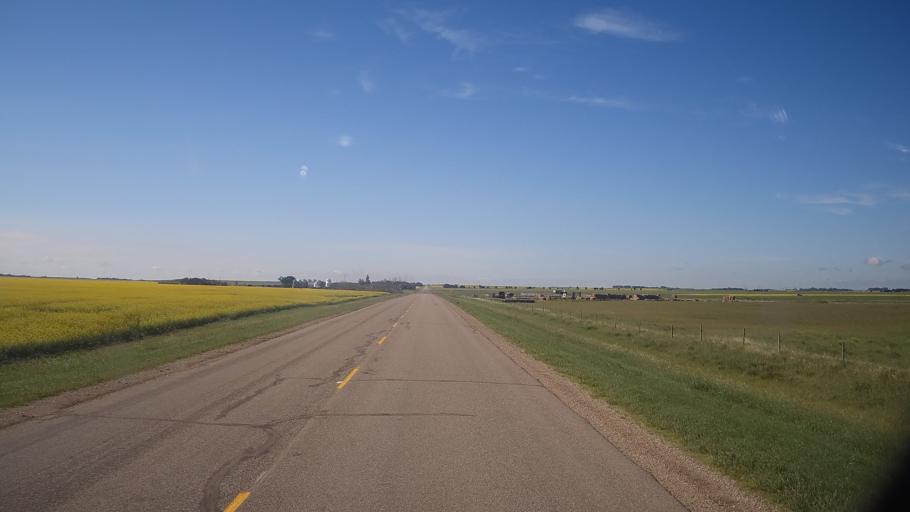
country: CA
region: Saskatchewan
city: Watrous
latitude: 51.6853
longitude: -105.3809
